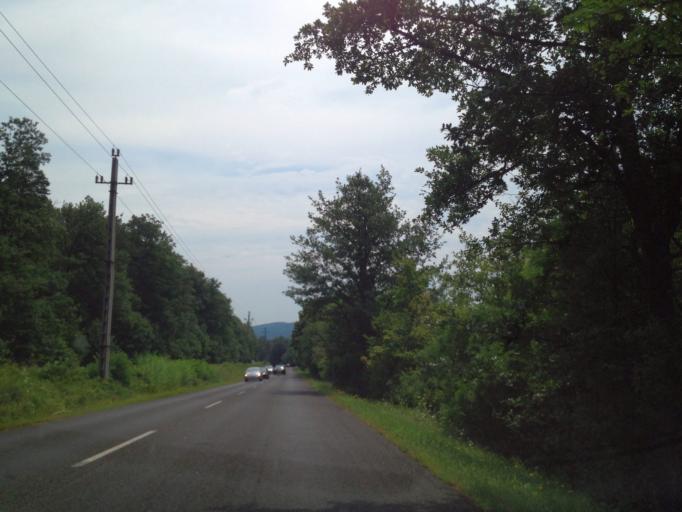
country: HU
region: Pest
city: Pilisszentkereszt
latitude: 47.7027
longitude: 18.8903
